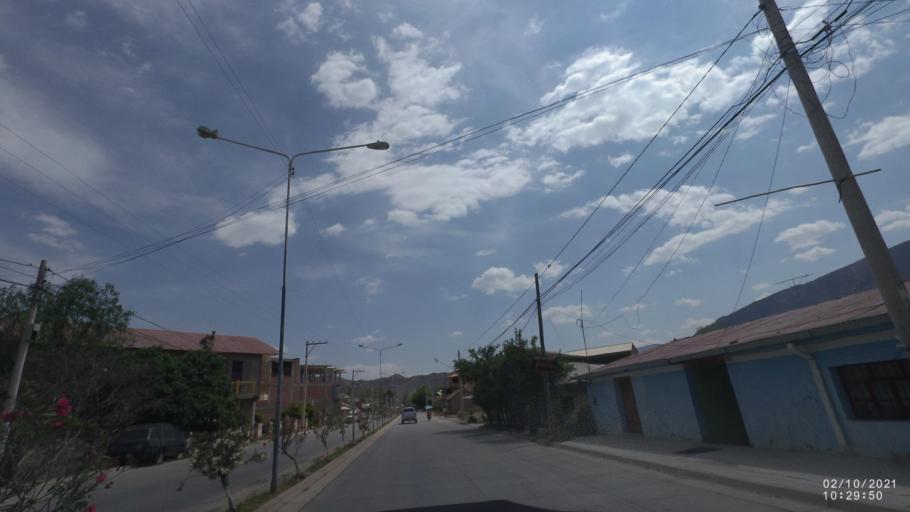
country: BO
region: Cochabamba
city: Capinota
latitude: -17.7020
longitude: -66.2661
